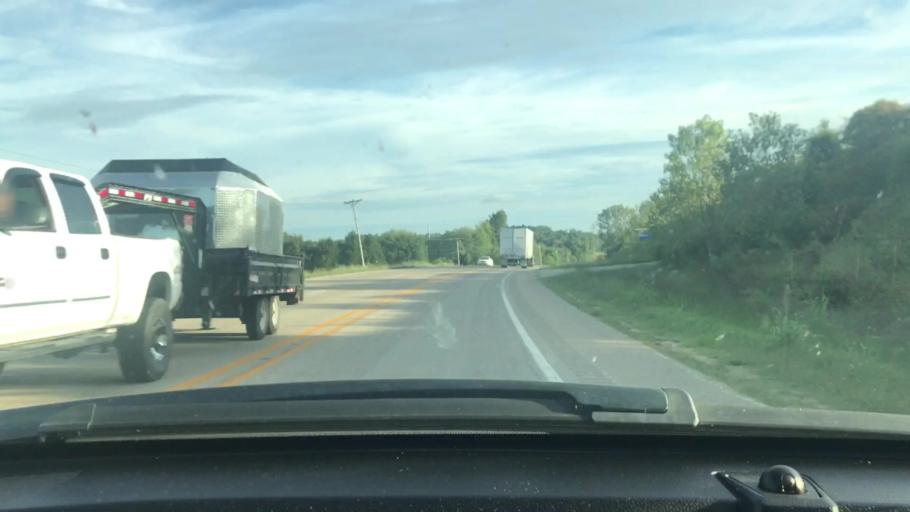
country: US
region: Arkansas
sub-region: Lawrence County
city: Hoxie
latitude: 36.1431
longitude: -91.1582
